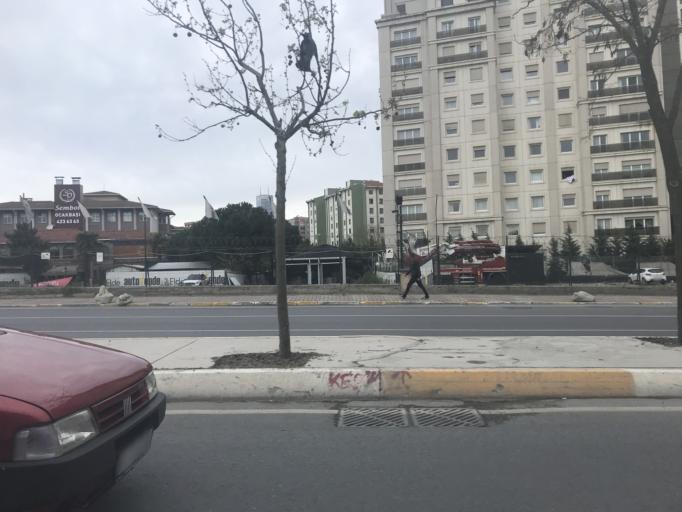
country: TR
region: Istanbul
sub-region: Atasehir
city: Atasehir
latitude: 40.9861
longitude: 29.1384
